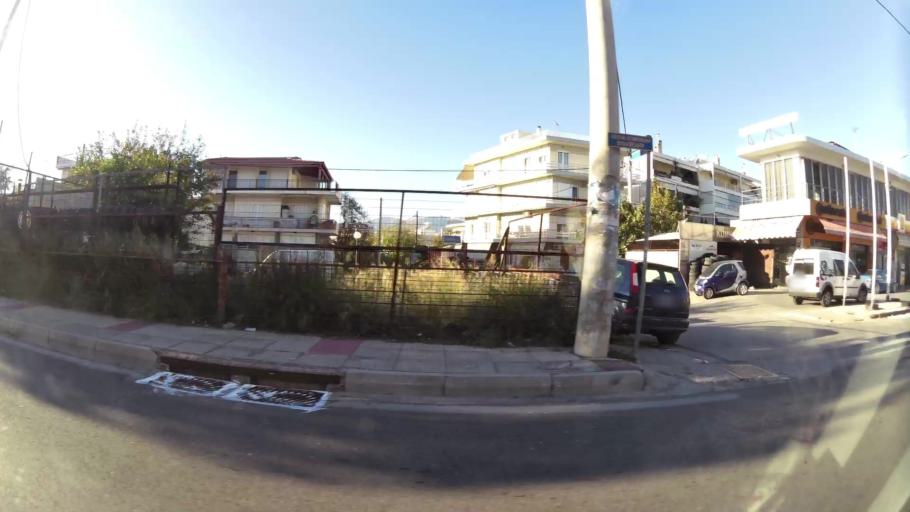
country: GR
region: Attica
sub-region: Nomarchia Athinas
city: Lykovrysi
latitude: 38.0702
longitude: 23.7837
